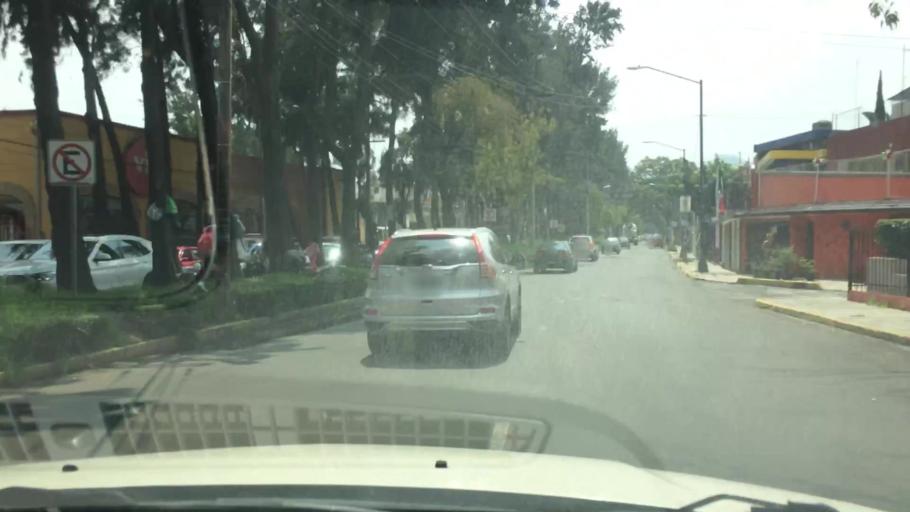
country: MX
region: Mexico City
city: Xochimilco
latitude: 19.2825
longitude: -99.1254
